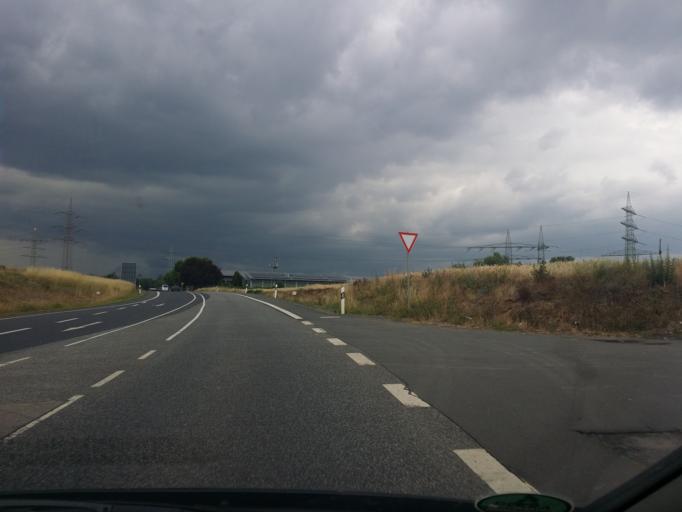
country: DE
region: Hesse
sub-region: Regierungsbezirk Darmstadt
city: Hofheim am Taunus
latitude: 50.0569
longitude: 8.4334
